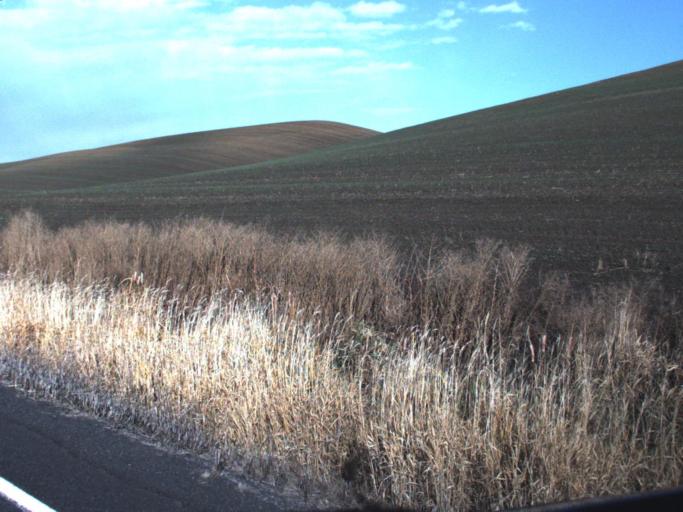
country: US
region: Washington
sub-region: Whitman County
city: Colfax
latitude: 46.7504
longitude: -117.3697
